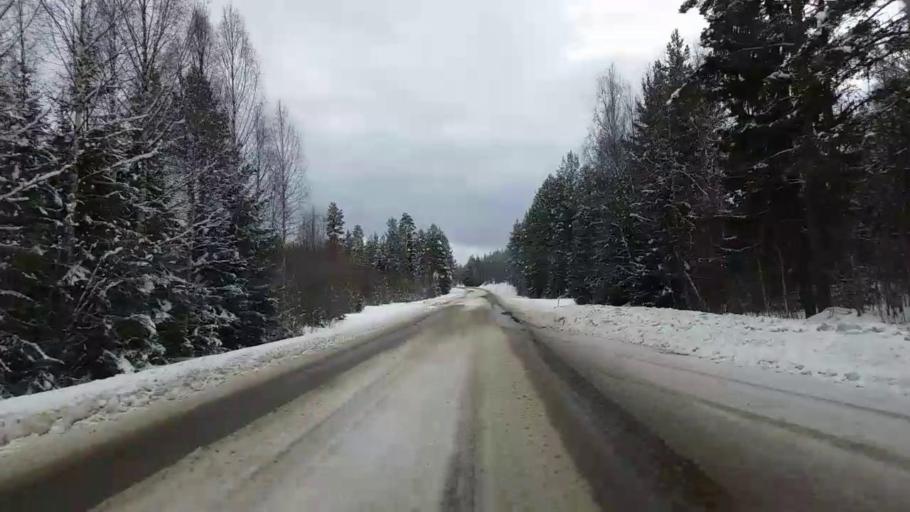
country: SE
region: Vaesternorrland
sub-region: Ange Kommun
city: Ange
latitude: 62.0748
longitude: 15.1016
